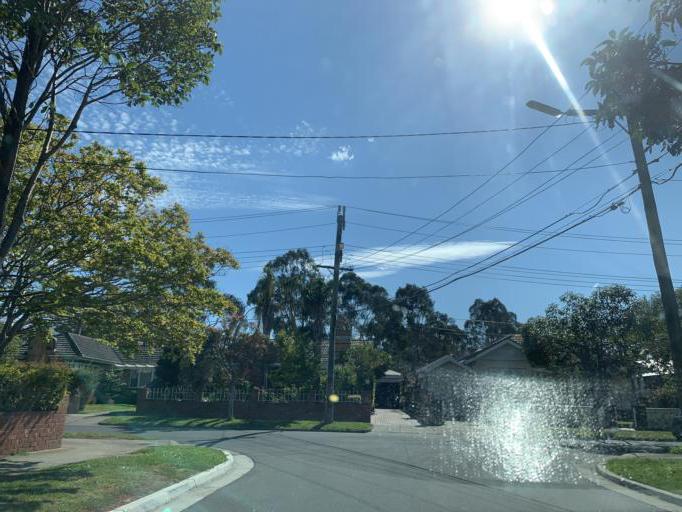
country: AU
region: Victoria
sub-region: Bayside
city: Hampton East
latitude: -37.9413
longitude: 145.0190
